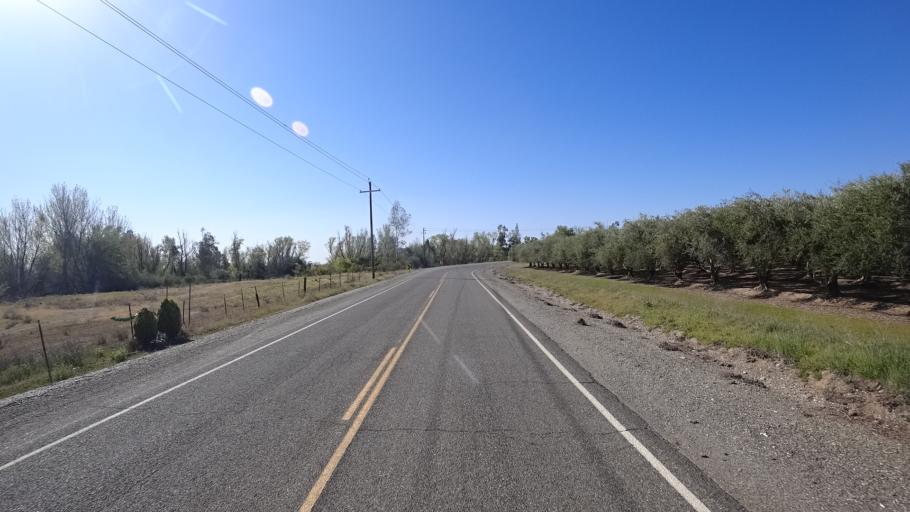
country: US
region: California
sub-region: Glenn County
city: Willows
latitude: 39.5441
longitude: -122.1651
